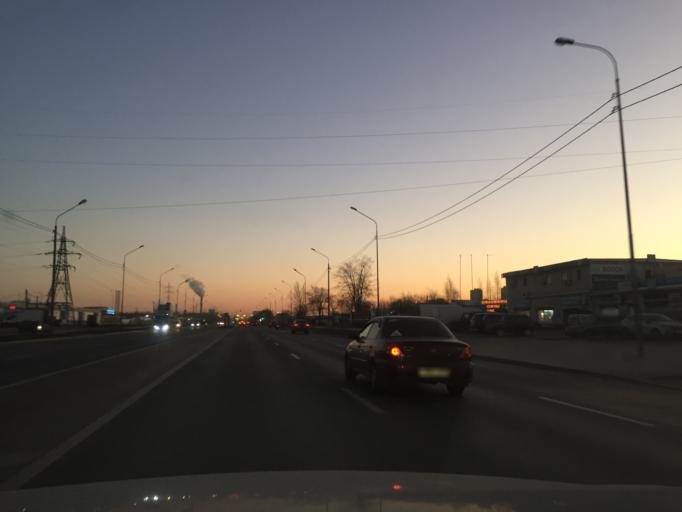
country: RU
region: St.-Petersburg
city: Obukhovo
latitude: 59.8614
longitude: 30.4189
